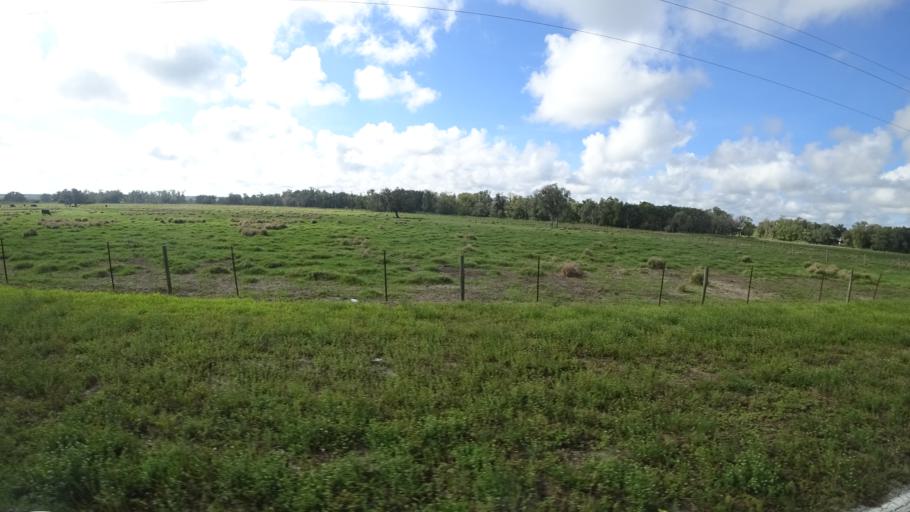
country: US
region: Florida
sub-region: Sarasota County
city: Lake Sarasota
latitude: 27.3461
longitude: -82.2397
